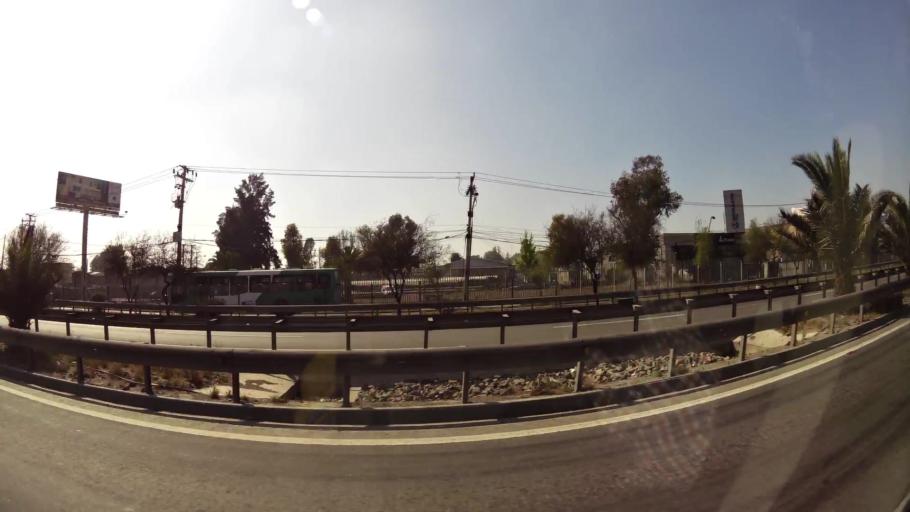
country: CL
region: Santiago Metropolitan
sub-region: Provincia de Santiago
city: Lo Prado
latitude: -33.3742
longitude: -70.7143
